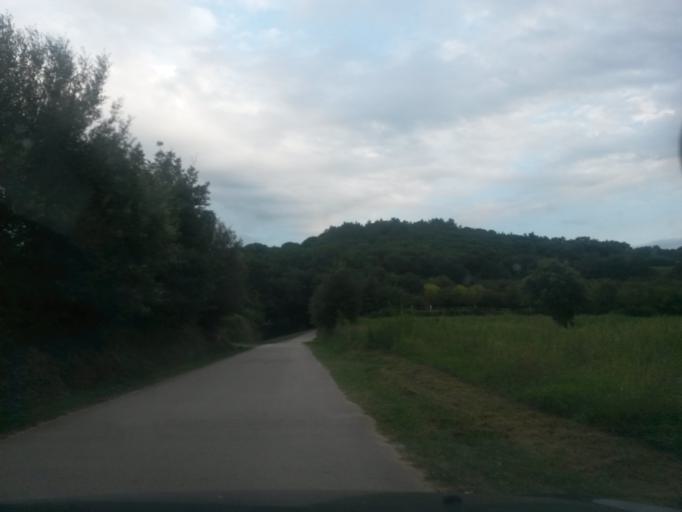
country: ES
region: Catalonia
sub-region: Provincia de Girona
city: Sant Gregori
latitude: 41.9755
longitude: 2.7037
